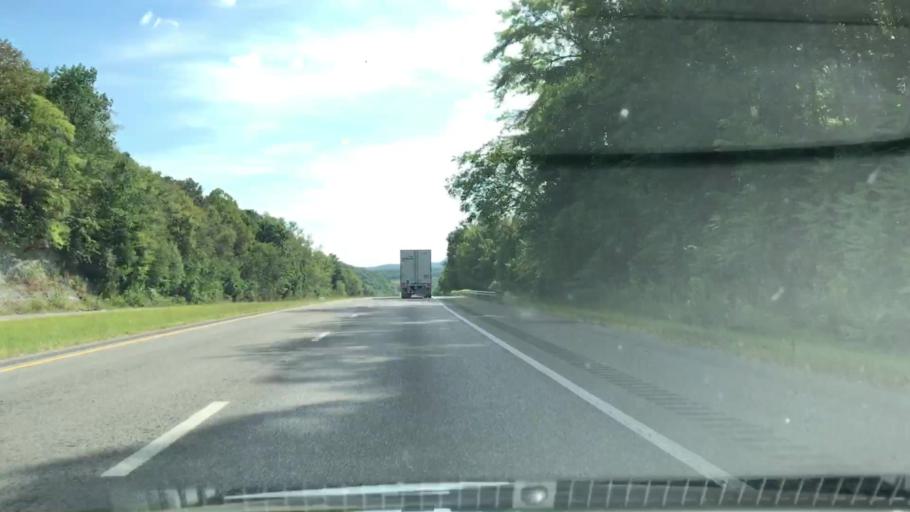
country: US
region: Alabama
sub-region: Limestone County
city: Ardmore
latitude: 35.1181
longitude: -86.8793
